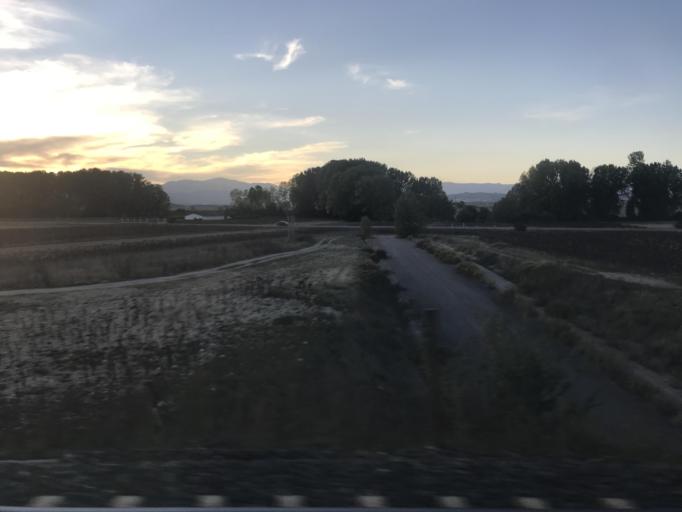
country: ES
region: Castille and Leon
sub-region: Provincia de Burgos
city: Miranda de Ebro
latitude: 42.6798
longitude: -2.9765
